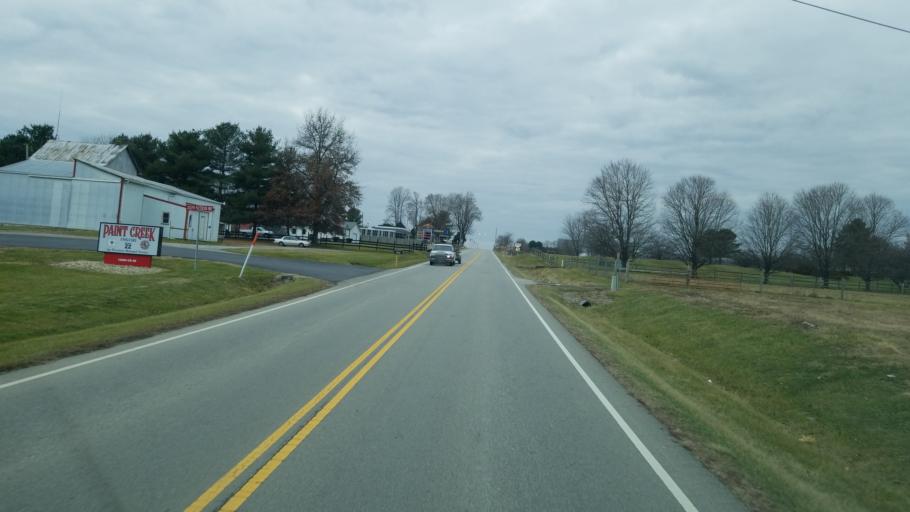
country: US
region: Ohio
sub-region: Highland County
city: Greenfield
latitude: 39.2182
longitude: -83.4345
